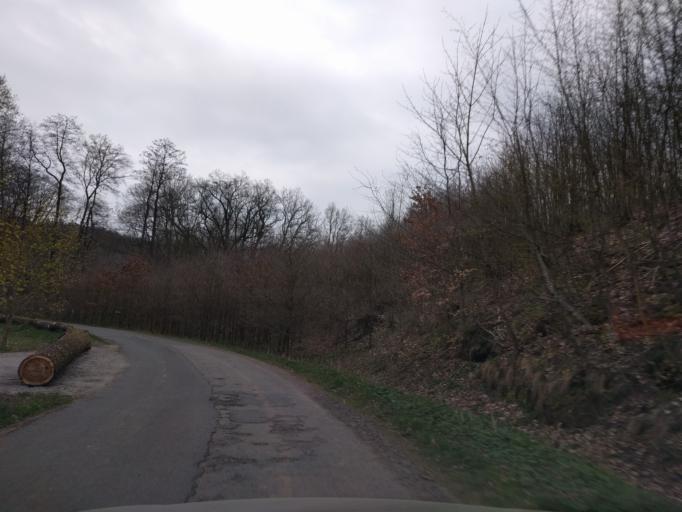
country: CZ
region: Central Bohemia
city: Kostelec nad Cernymi Lesy
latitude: 50.0201
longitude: 14.8138
